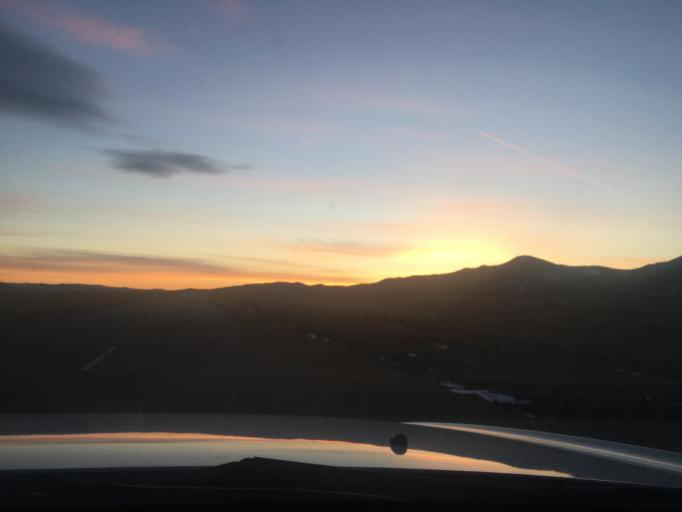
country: MN
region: Central Aimak
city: Mandal
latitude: 48.0942
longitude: 106.6089
